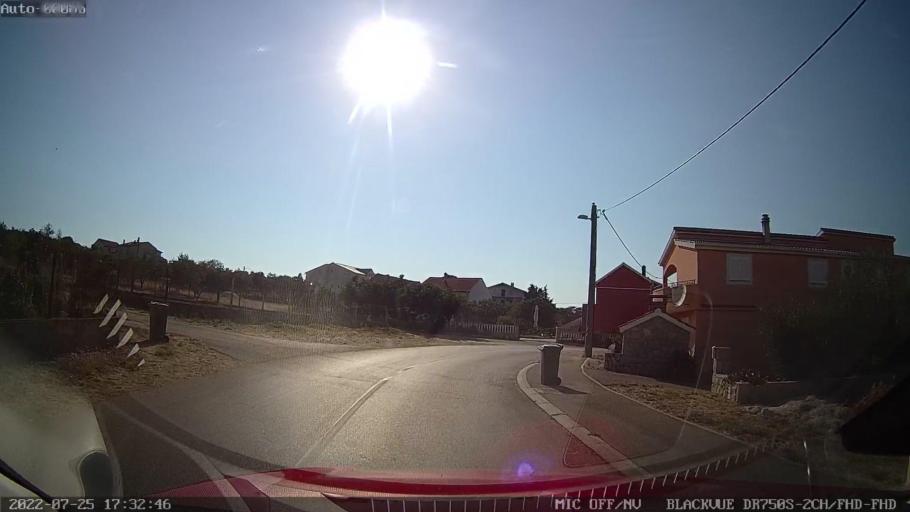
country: HR
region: Zadarska
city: Posedarje
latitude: 44.1782
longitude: 15.4901
